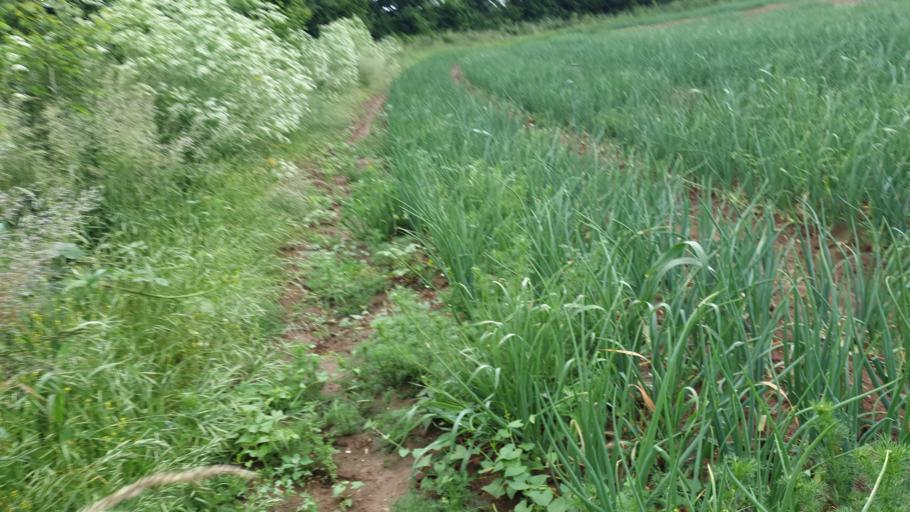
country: GB
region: England
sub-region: Essex
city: Alresford
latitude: 51.8633
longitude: 1.0317
